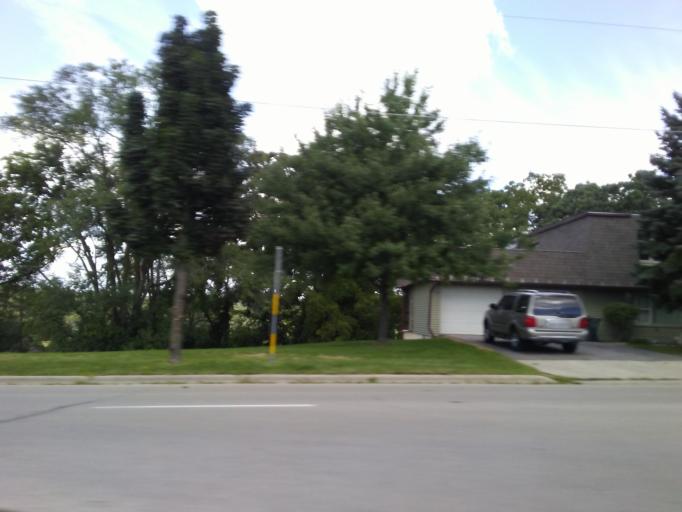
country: US
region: Wisconsin
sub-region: Dane County
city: Verona
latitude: 43.0306
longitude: -89.5081
